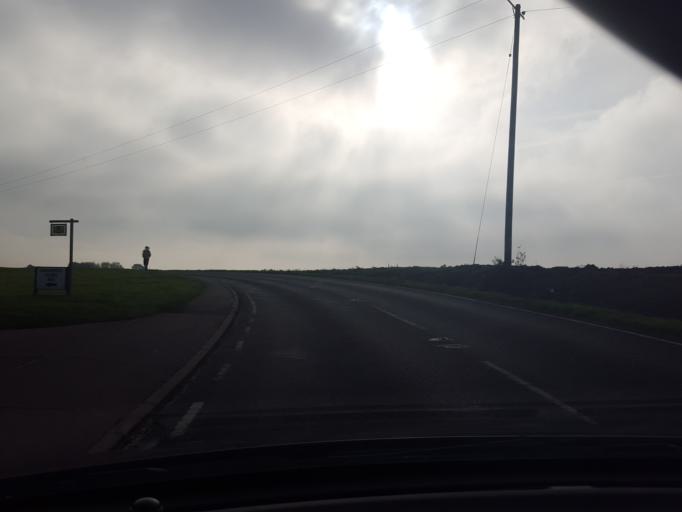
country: GB
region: England
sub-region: Essex
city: Mistley
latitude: 51.9385
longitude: 1.1127
